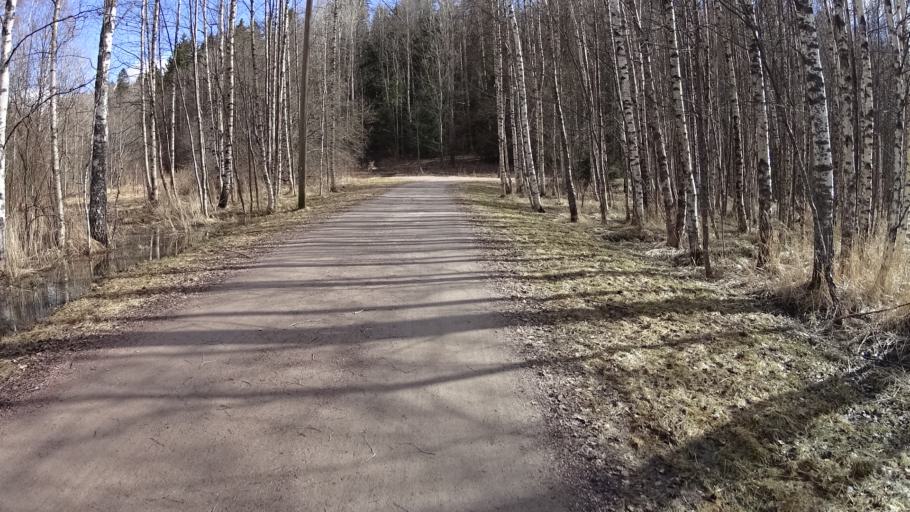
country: FI
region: Uusimaa
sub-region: Helsinki
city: Espoo
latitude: 60.2152
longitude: 24.6779
